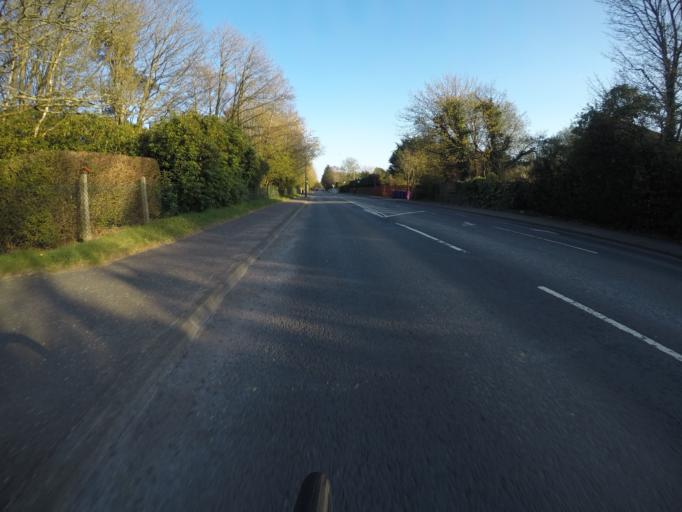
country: GB
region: Scotland
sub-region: North Ayrshire
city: Irvine
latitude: 55.6343
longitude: -4.6780
